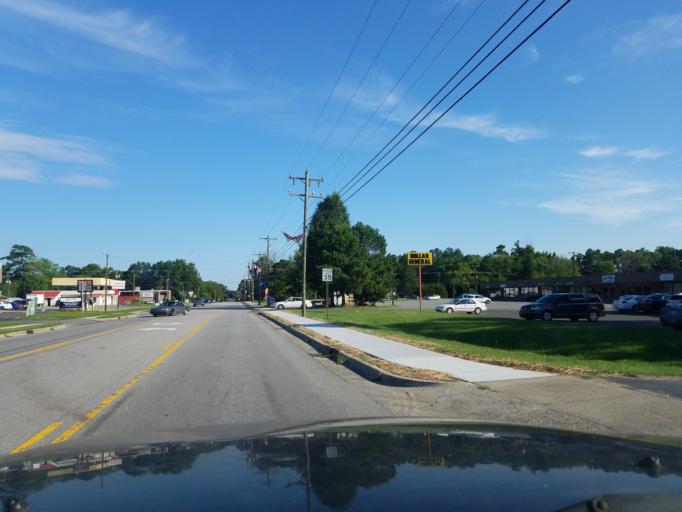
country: US
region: North Carolina
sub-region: Granville County
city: Butner
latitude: 36.1340
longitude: -78.7583
